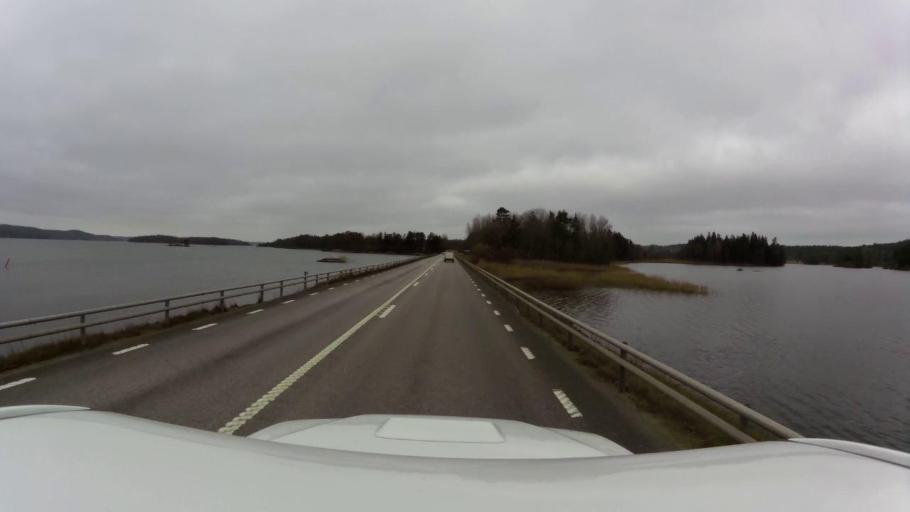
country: SE
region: OEstergoetland
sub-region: Kinda Kommun
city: Rimforsa
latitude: 58.1526
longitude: 15.6801
